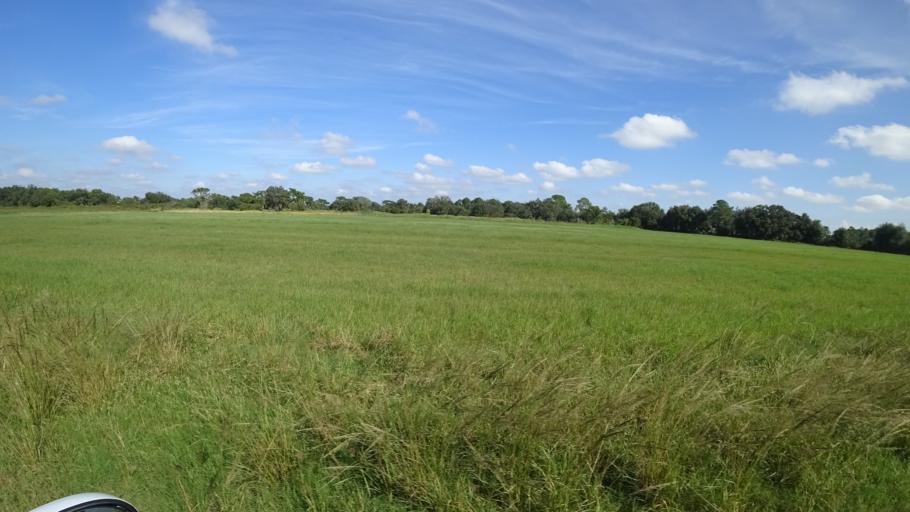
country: US
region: Florida
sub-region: Sarasota County
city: Lake Sarasota
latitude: 27.3622
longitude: -82.1559
